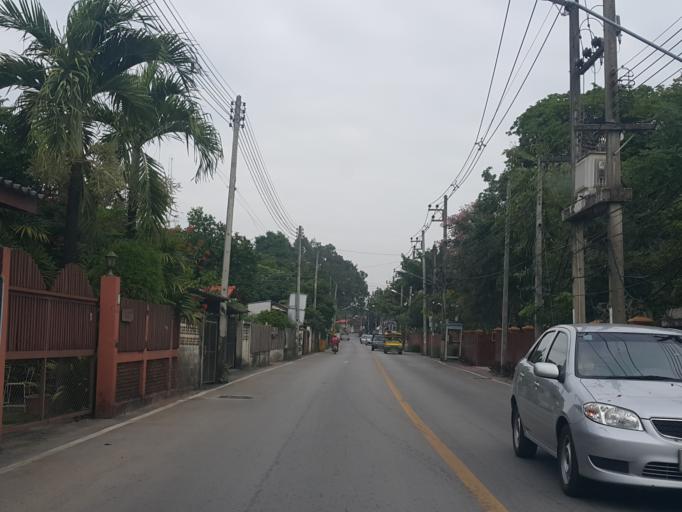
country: TH
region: Lampang
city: Lampang
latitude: 18.2944
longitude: 99.5091
